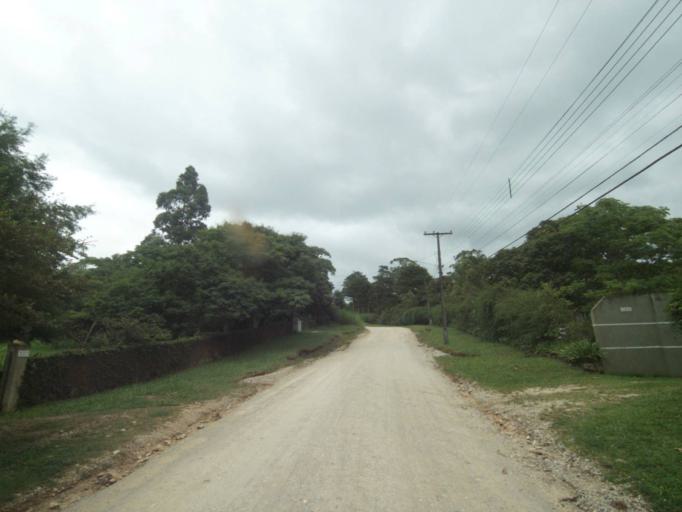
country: BR
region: Parana
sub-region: Campina Grande Do Sul
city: Campina Grande do Sul
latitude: -25.3223
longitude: -49.0816
